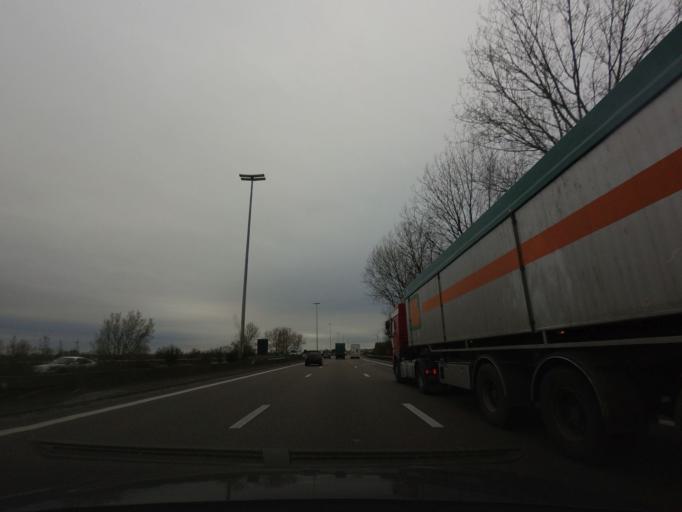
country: BE
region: Flanders
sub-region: Provincie Oost-Vlaanderen
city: Lokeren
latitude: 51.0816
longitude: 4.0109
